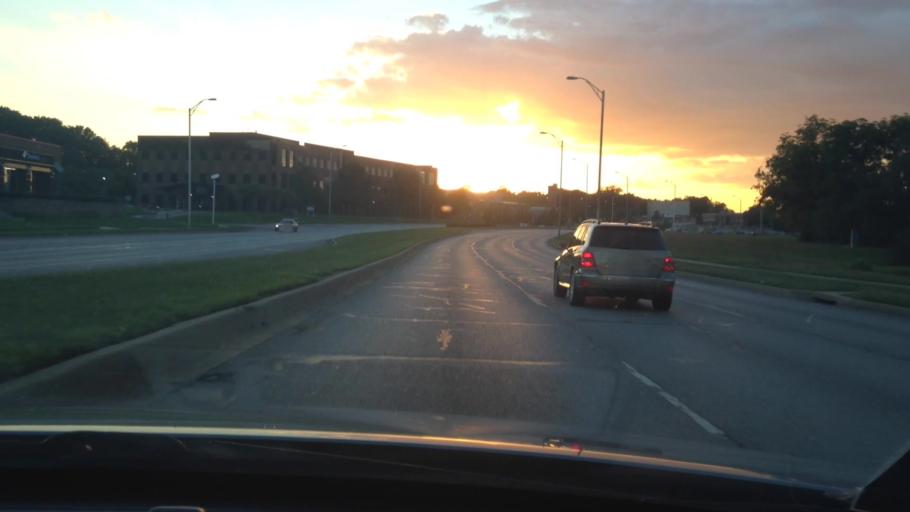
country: US
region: Missouri
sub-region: Jackson County
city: Raytown
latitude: 39.0348
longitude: -94.5345
